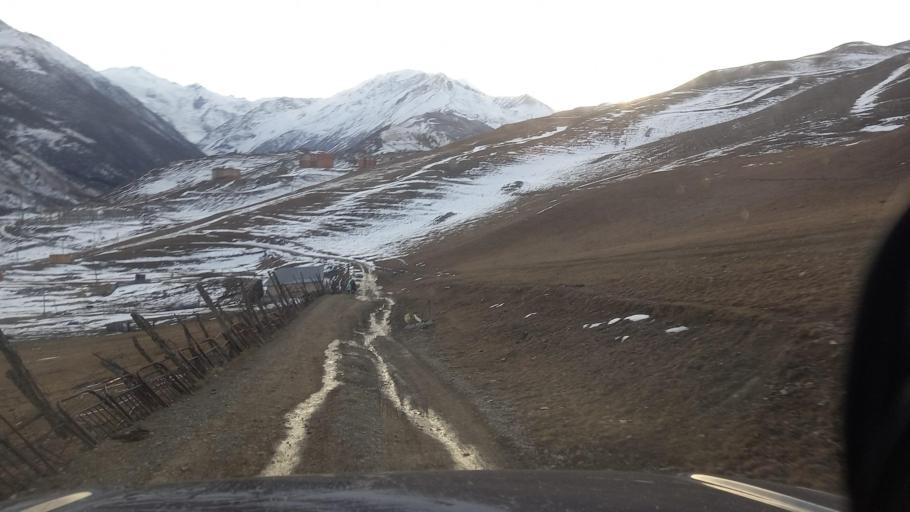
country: RU
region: Ingushetiya
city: Dzhayrakh
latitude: 42.8509
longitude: 44.5138
